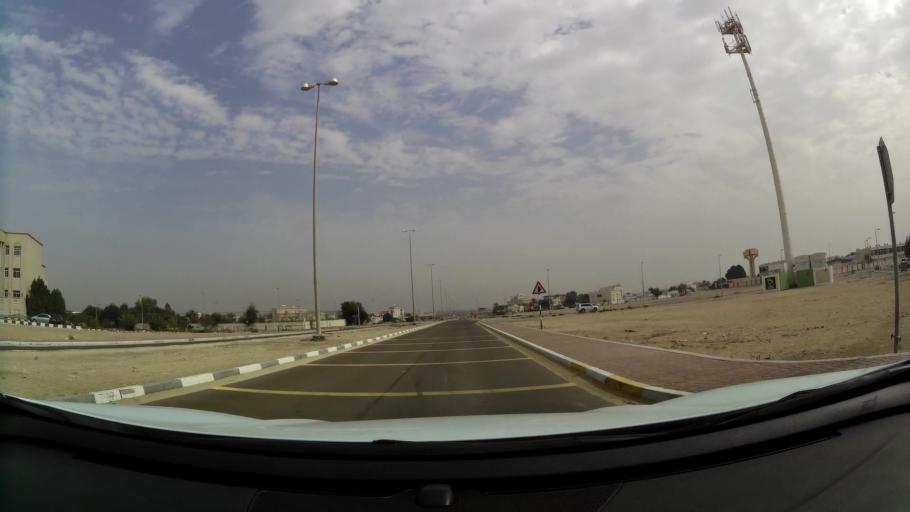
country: AE
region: Abu Dhabi
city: Abu Dhabi
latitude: 24.3185
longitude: 54.6378
